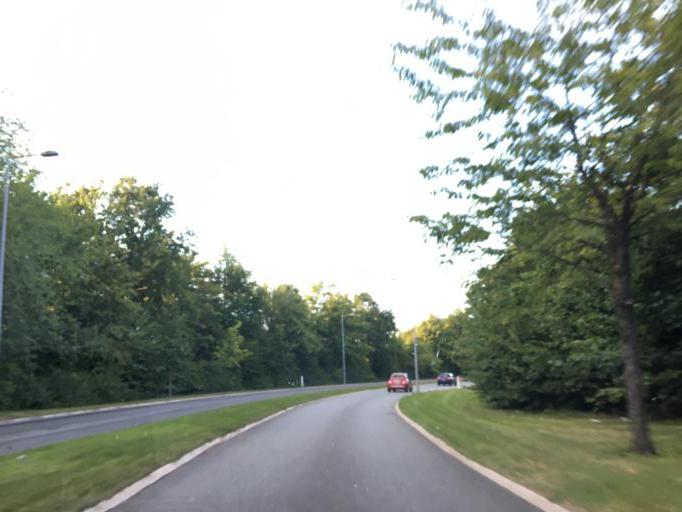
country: DK
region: Capital Region
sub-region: Horsholm Kommune
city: Horsholm
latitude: 55.8810
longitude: 12.4939
